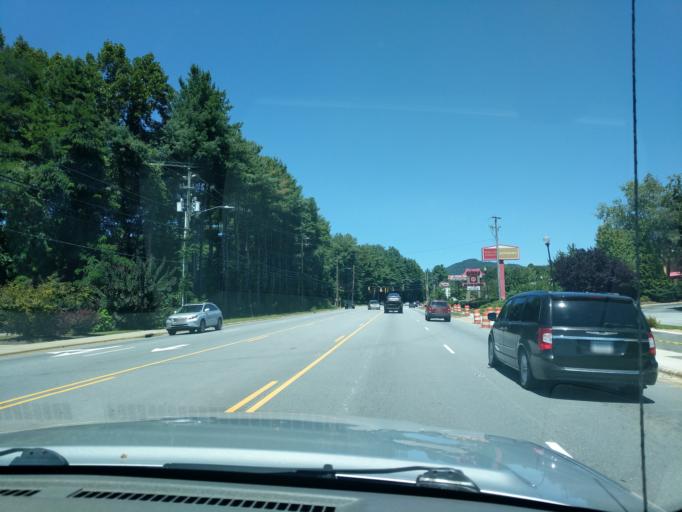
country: US
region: North Carolina
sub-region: Buncombe County
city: Royal Pines
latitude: 35.4898
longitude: -82.5238
